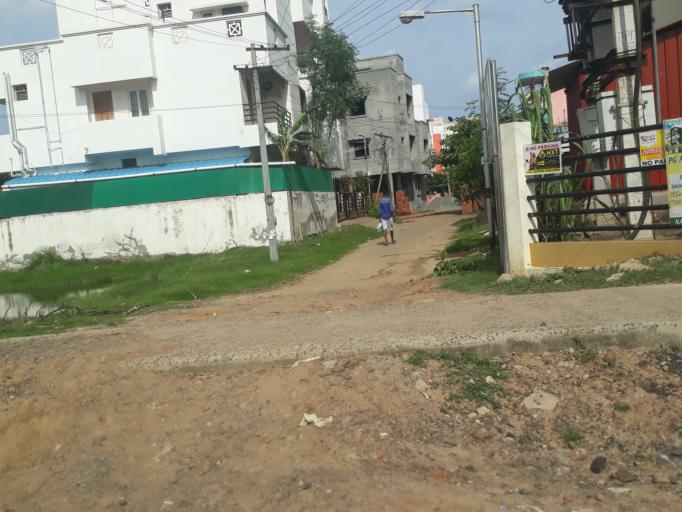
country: IN
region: Tamil Nadu
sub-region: Kancheepuram
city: Perungudi
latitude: 12.9510
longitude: 80.2352
